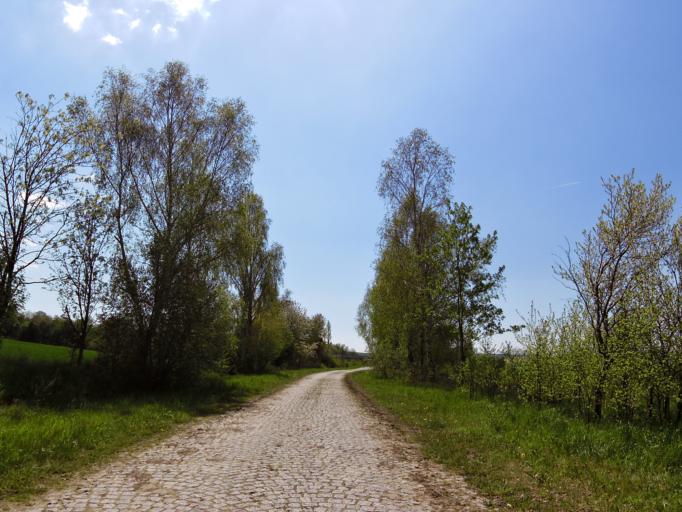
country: DE
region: Thuringia
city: Marksuhl
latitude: 50.9014
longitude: 10.2243
